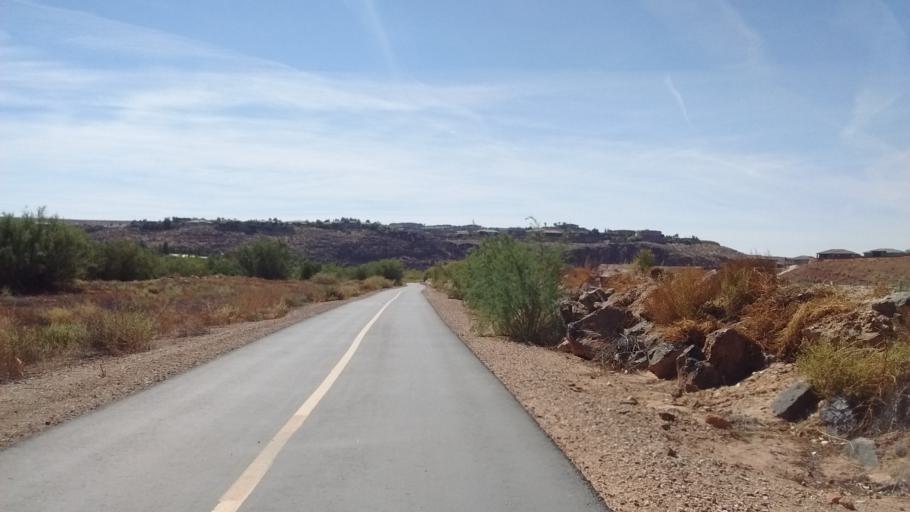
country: US
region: Utah
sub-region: Washington County
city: Saint George
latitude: 37.0913
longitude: -113.5377
